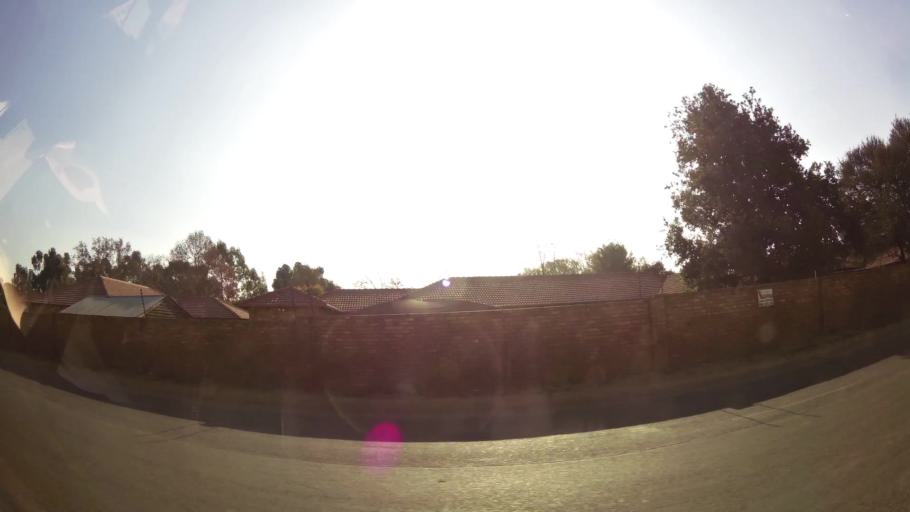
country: ZA
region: Gauteng
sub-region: West Rand District Municipality
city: Randfontein
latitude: -26.1632
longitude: 27.7098
